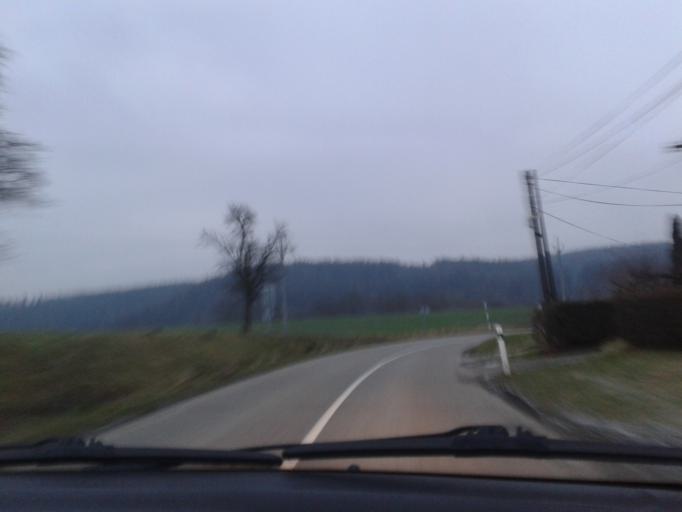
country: CZ
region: Olomoucky
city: Namest' na Hane
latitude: 49.5836
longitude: 17.0105
